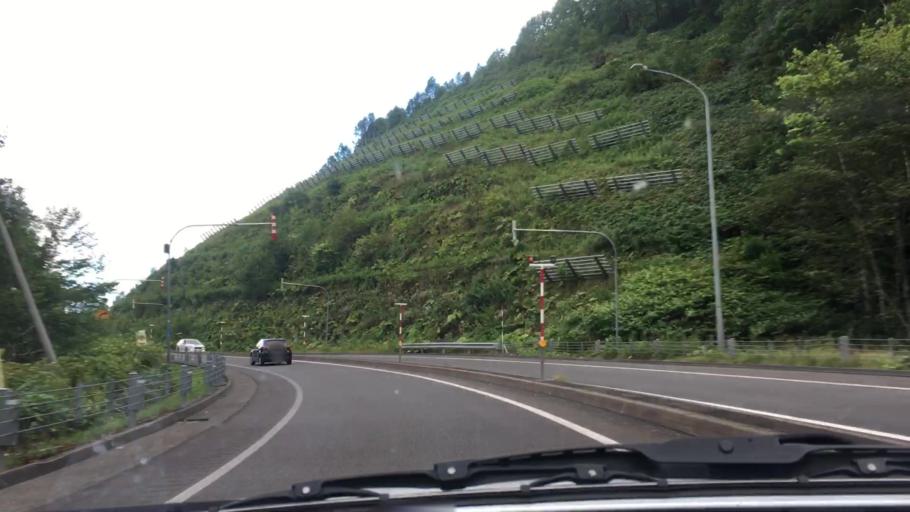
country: JP
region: Hokkaido
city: Shimo-furano
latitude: 43.1498
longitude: 142.7732
